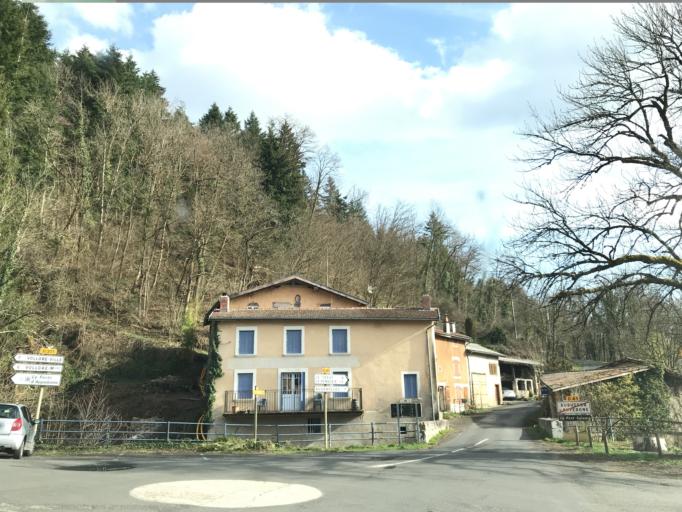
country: FR
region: Auvergne
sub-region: Departement du Puy-de-Dome
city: Courpiere
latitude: 45.7551
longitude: 3.6190
